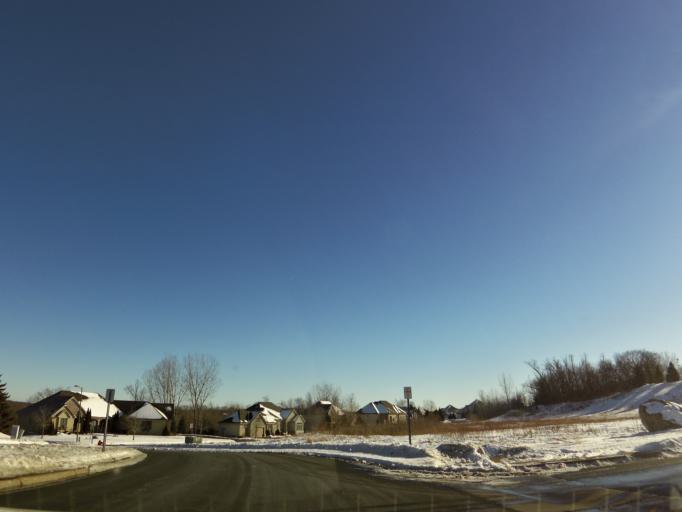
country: US
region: Minnesota
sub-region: Scott County
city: Prior Lake
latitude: 44.7393
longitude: -93.4576
